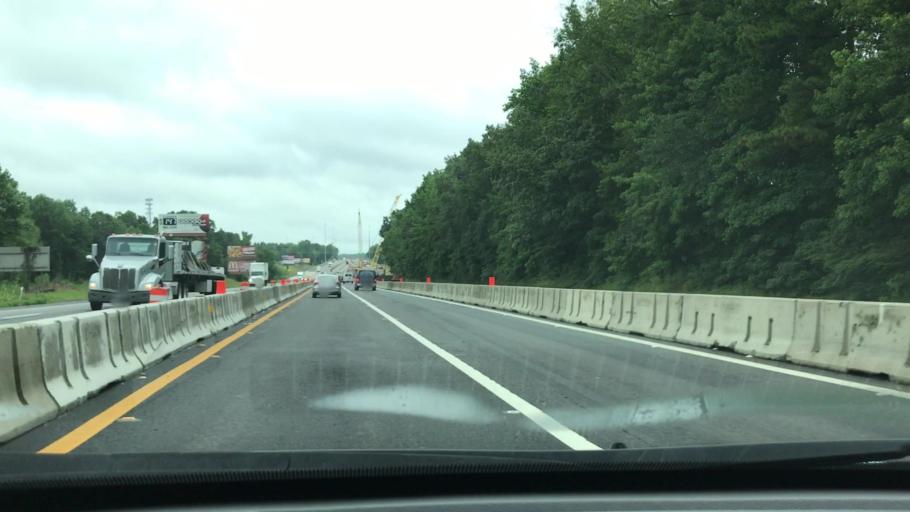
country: US
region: Virginia
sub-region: City of Emporia
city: Emporia
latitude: 36.6910
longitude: -77.5560
